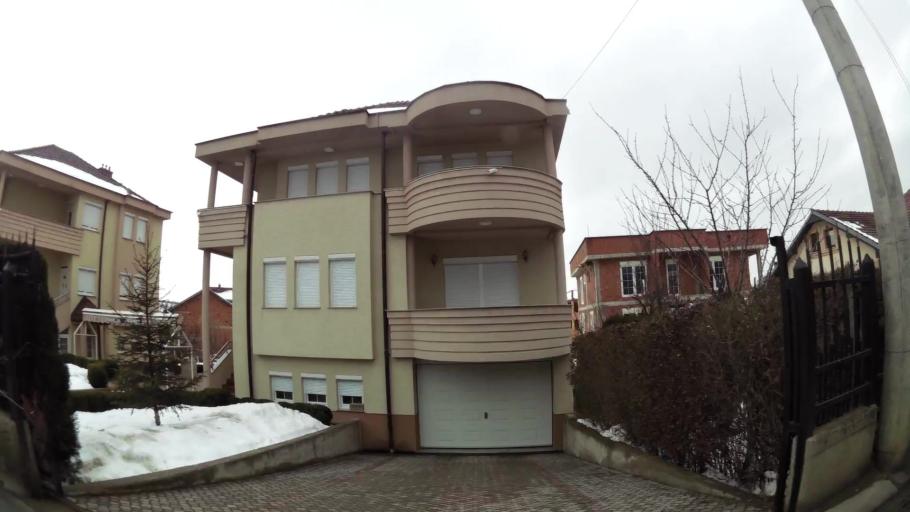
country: XK
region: Pristina
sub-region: Komuna e Prishtines
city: Pristina
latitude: 42.6454
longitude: 21.1871
